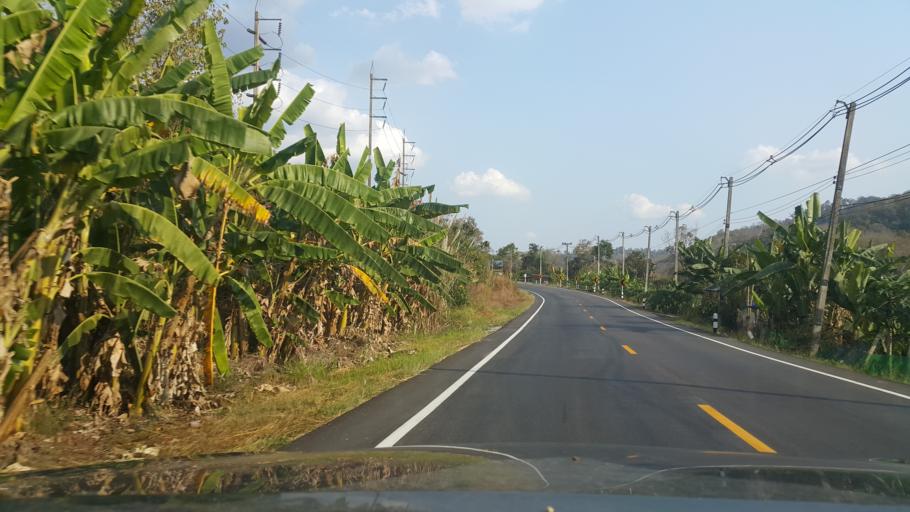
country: TH
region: Loei
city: Dan Sai
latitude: 17.2311
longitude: 101.0807
